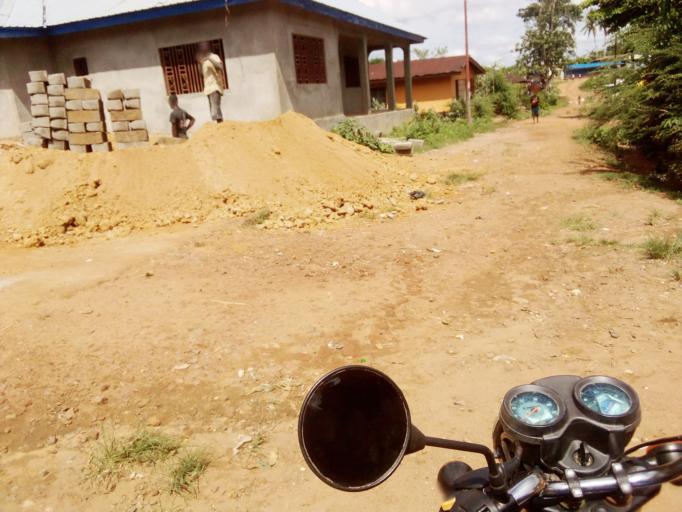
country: SL
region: Western Area
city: Waterloo
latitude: 8.3369
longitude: -13.0697
